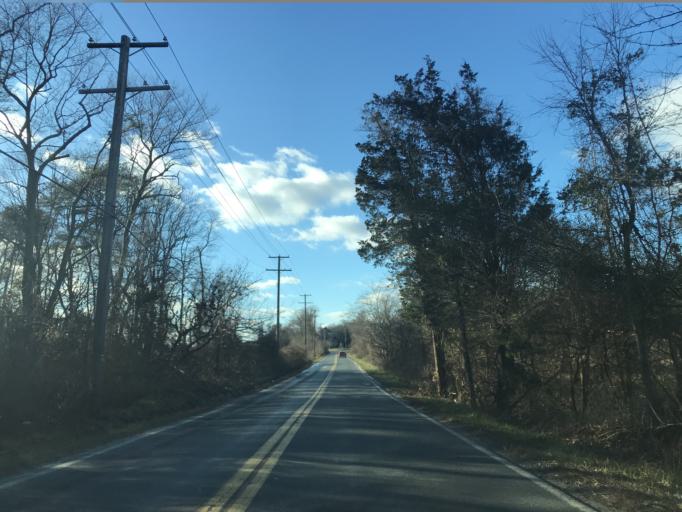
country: US
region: Maryland
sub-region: Baltimore County
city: Bowleys Quarters
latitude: 39.3633
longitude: -76.3952
